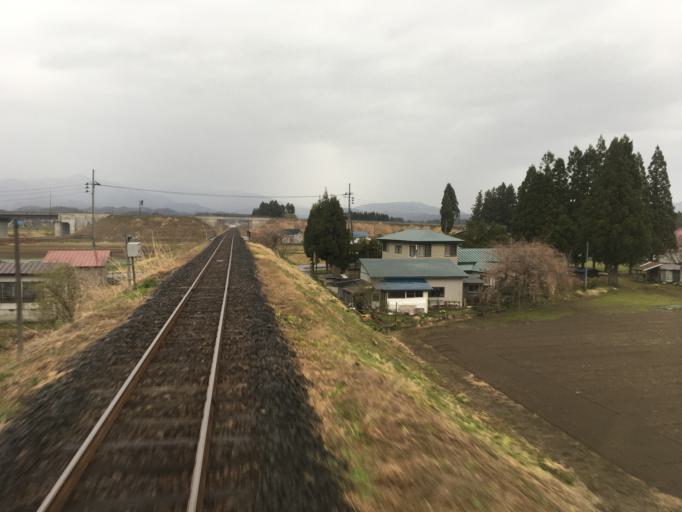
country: JP
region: Akita
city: Kakunodatemachi
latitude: 39.6111
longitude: 140.5778
